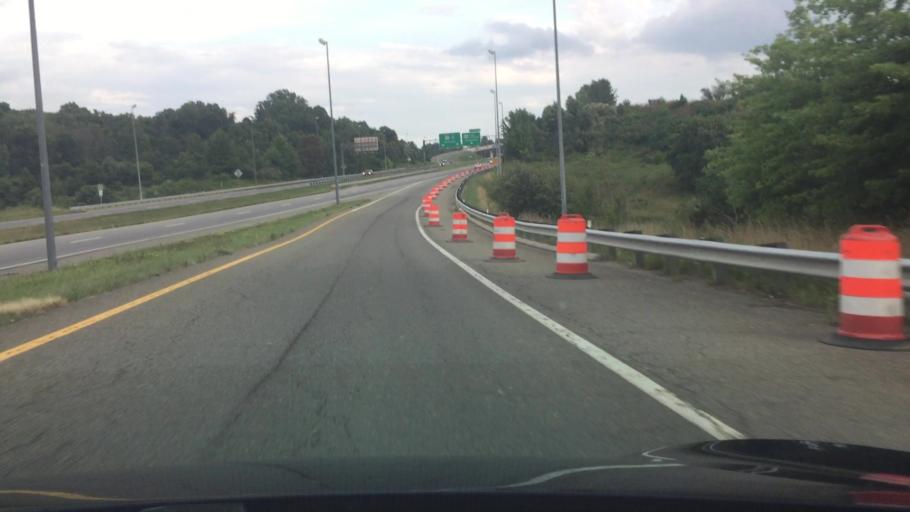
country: US
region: Virginia
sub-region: Montgomery County
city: Merrimac
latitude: 37.1627
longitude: -80.4145
